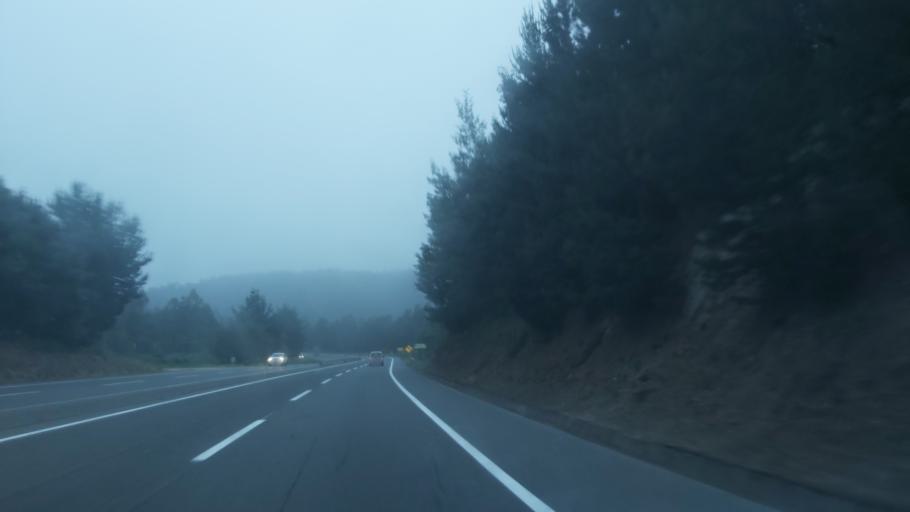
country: CL
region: Biobio
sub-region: Provincia de Concepcion
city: Penco
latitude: -36.7384
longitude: -72.8964
